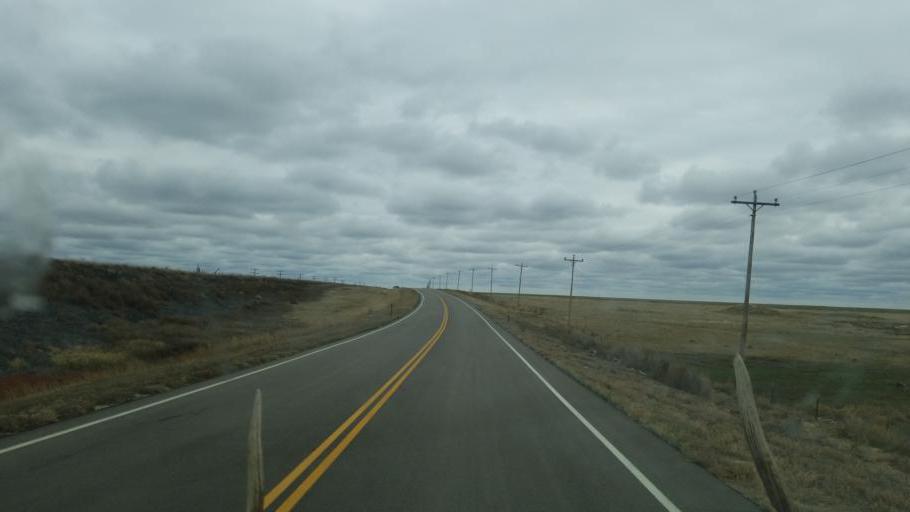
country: US
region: Colorado
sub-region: Kiowa County
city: Eads
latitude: 38.4986
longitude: -102.9818
